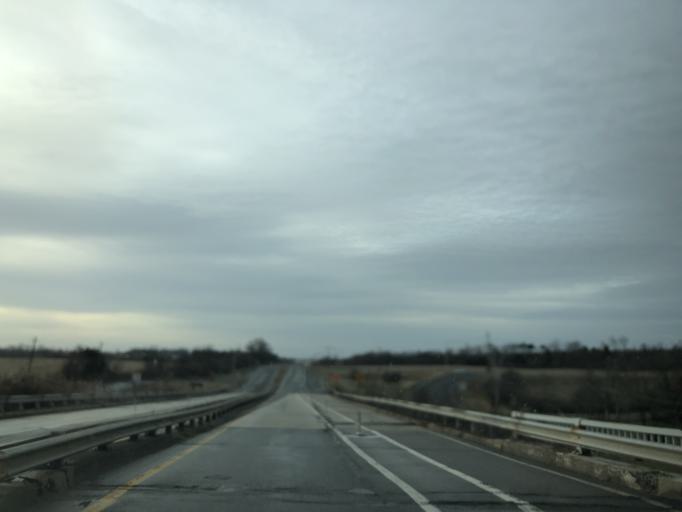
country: US
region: Delaware
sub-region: New Castle County
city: Delaware City
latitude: 39.5474
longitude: -75.6488
